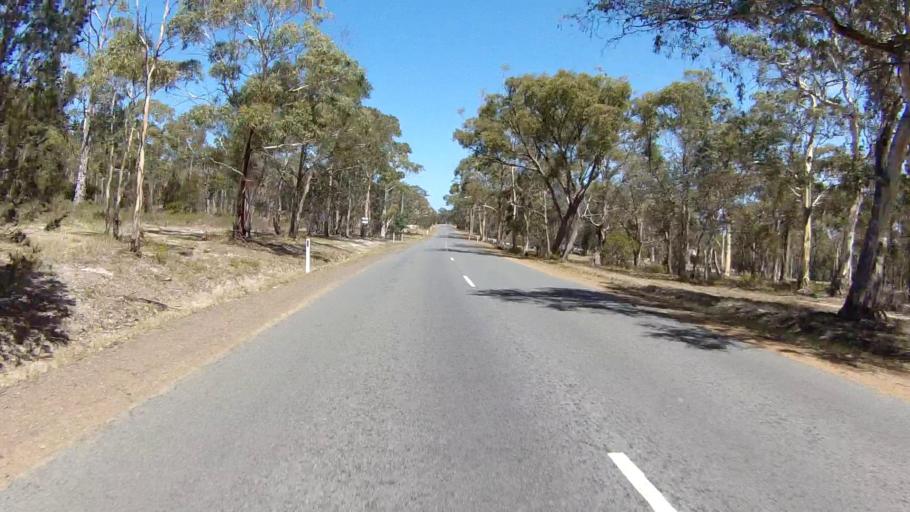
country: AU
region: Tasmania
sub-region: Clarence
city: Sandford
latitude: -42.9718
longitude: 147.4801
